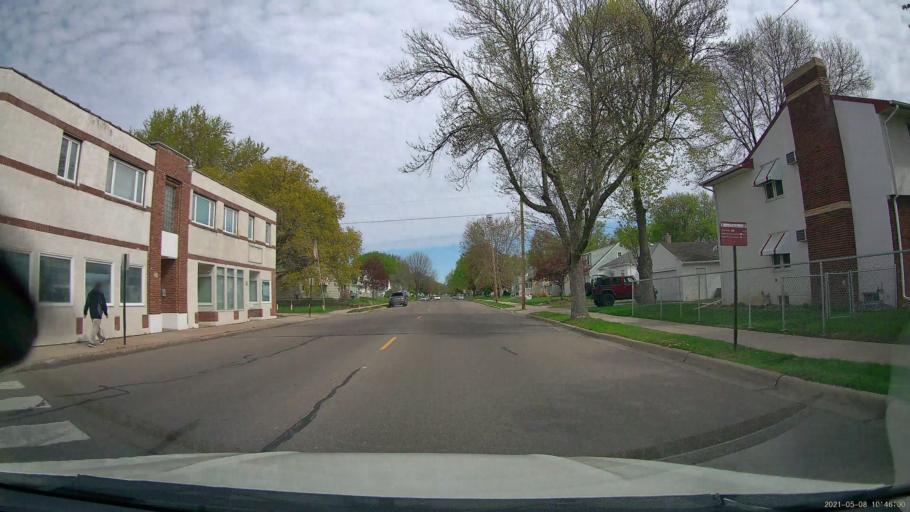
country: US
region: Minnesota
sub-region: Dakota County
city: South Saint Paul
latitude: 44.8963
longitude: -93.0526
